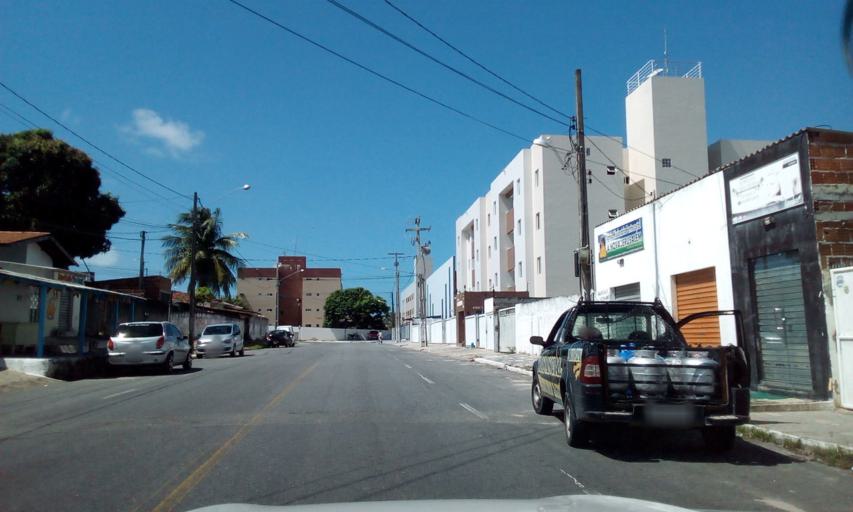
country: BR
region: Paraiba
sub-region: Joao Pessoa
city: Joao Pessoa
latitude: -7.1870
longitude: -34.8442
